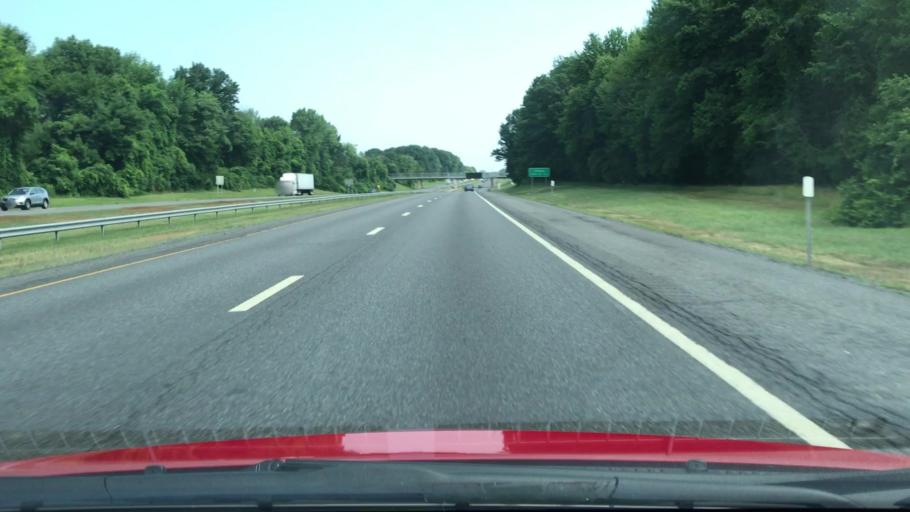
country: US
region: New York
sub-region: Albany County
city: Delmar
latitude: 42.5953
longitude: -73.7853
